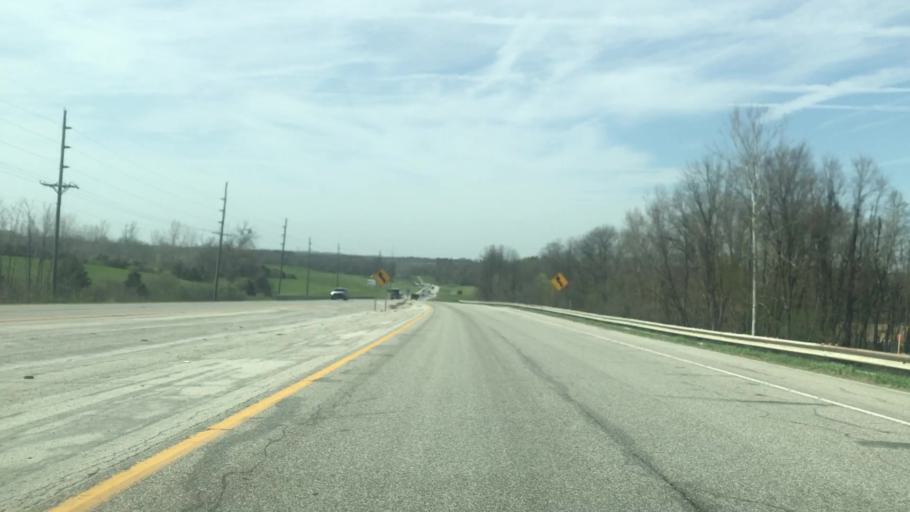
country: US
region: Indiana
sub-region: Putnam County
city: Cloverdale
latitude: 39.5401
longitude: -86.8045
